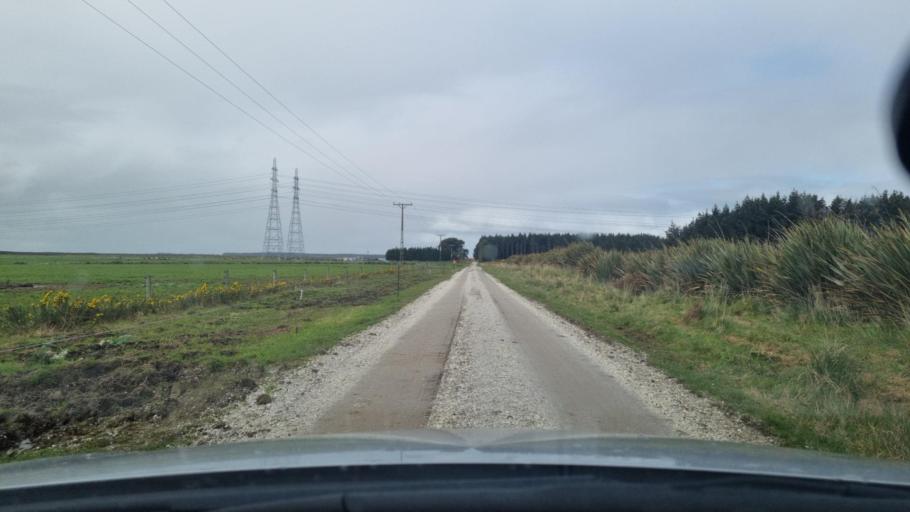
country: NZ
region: Southland
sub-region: Invercargill City
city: Invercargill
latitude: -46.4920
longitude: 168.4314
